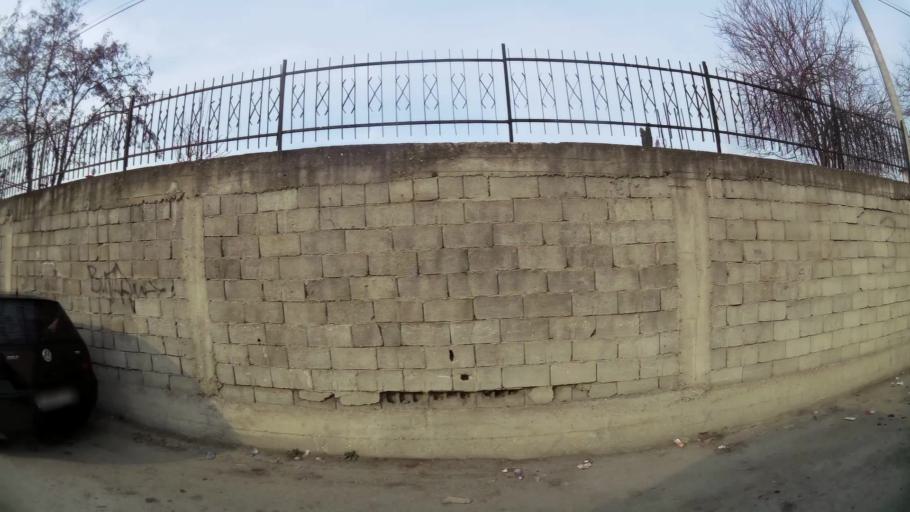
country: MK
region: Cair
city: Cair
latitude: 42.0145
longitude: 21.4388
